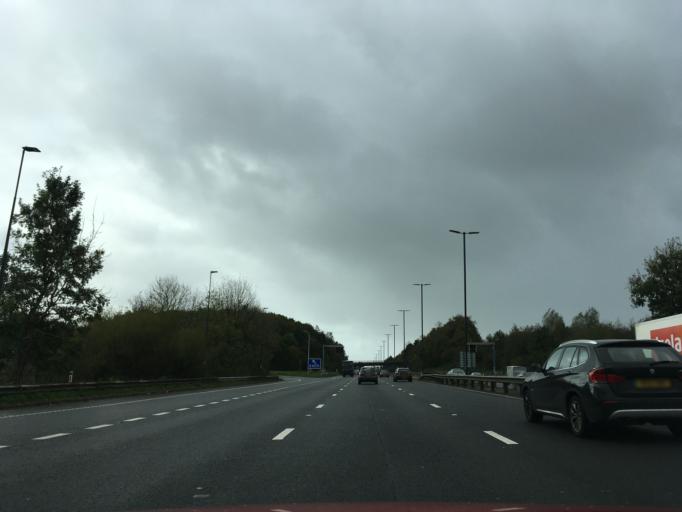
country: GB
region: Wales
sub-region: Newport
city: Newport
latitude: 51.5883
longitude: -3.0322
